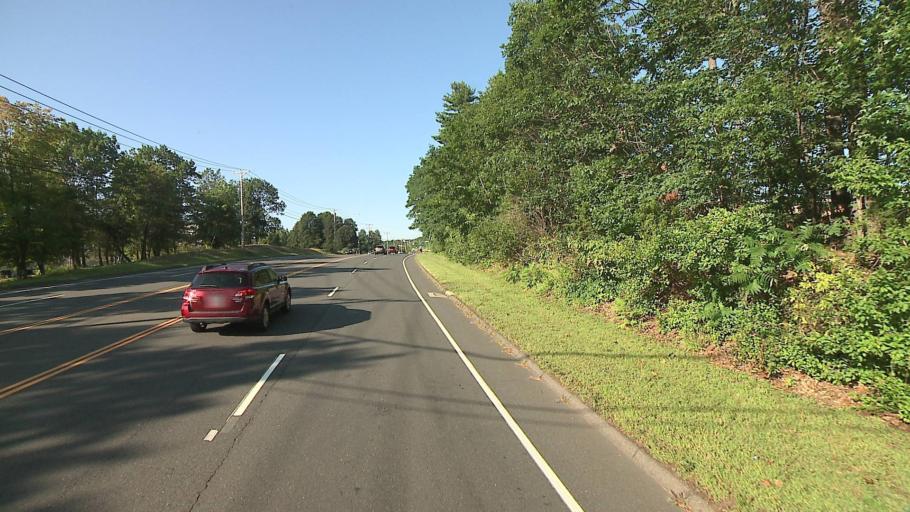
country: US
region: Connecticut
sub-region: Hartford County
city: Farmington
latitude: 41.7319
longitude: -72.7985
